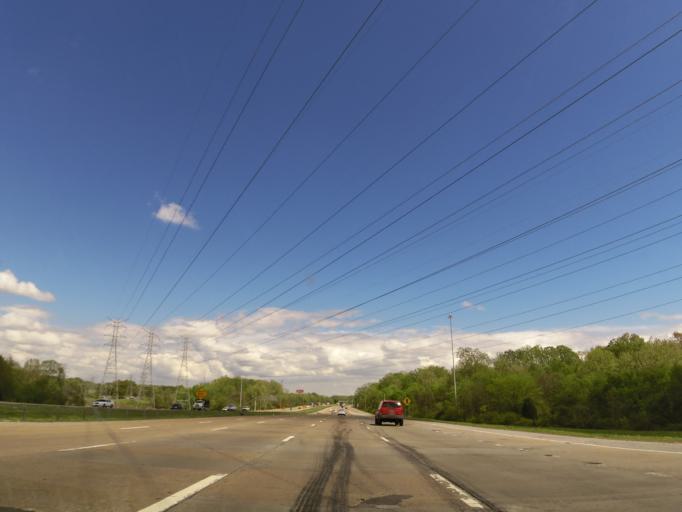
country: US
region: Tennessee
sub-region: Shelby County
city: Memphis
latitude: 35.1917
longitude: -90.0069
